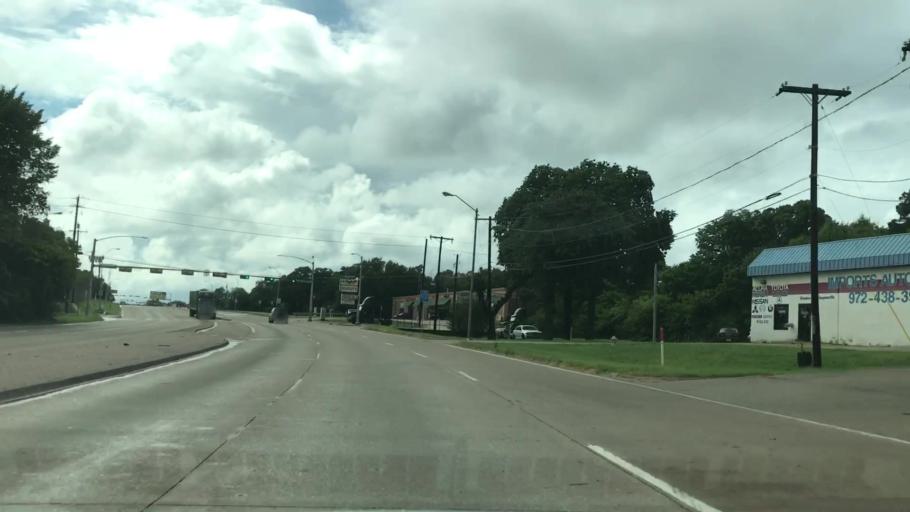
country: US
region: Texas
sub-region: Dallas County
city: Irving
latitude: 32.8096
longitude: -96.9157
